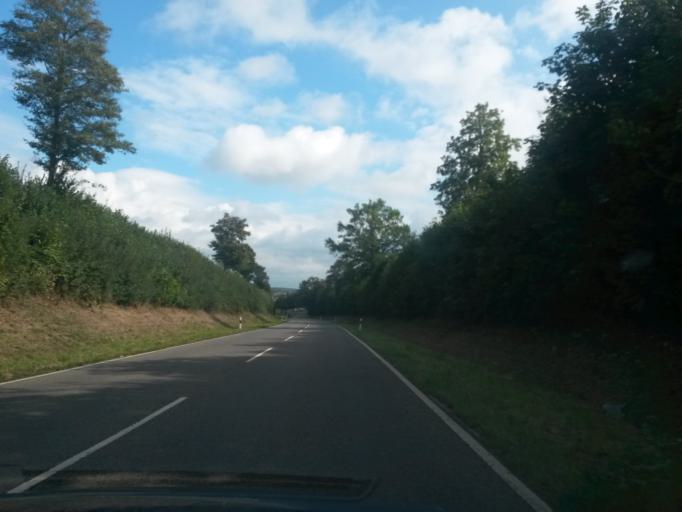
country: DE
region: Baden-Wuerttemberg
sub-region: Karlsruhe Region
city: Ettlingen
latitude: 48.9181
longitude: 8.4929
